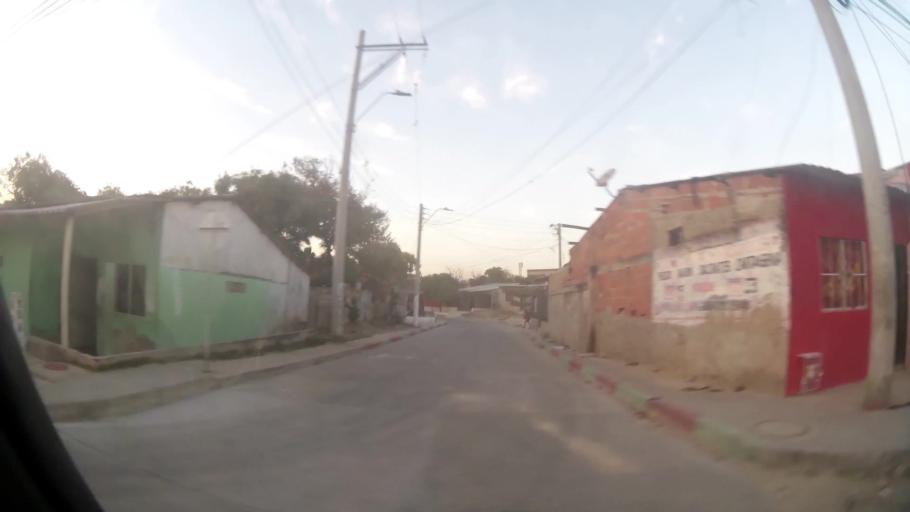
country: CO
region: Atlantico
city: Barranquilla
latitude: 10.9576
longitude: -74.8317
